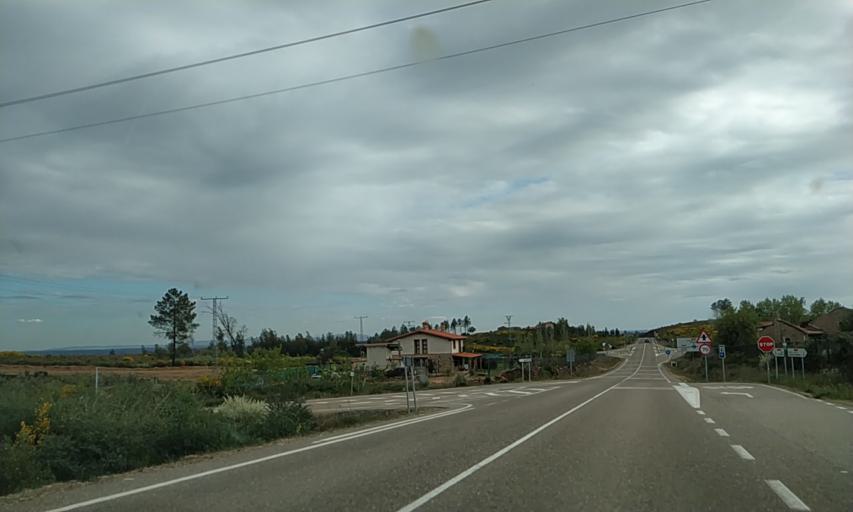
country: ES
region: Extremadura
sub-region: Provincia de Caceres
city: Perales del Puerto
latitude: 40.1853
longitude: -6.6758
